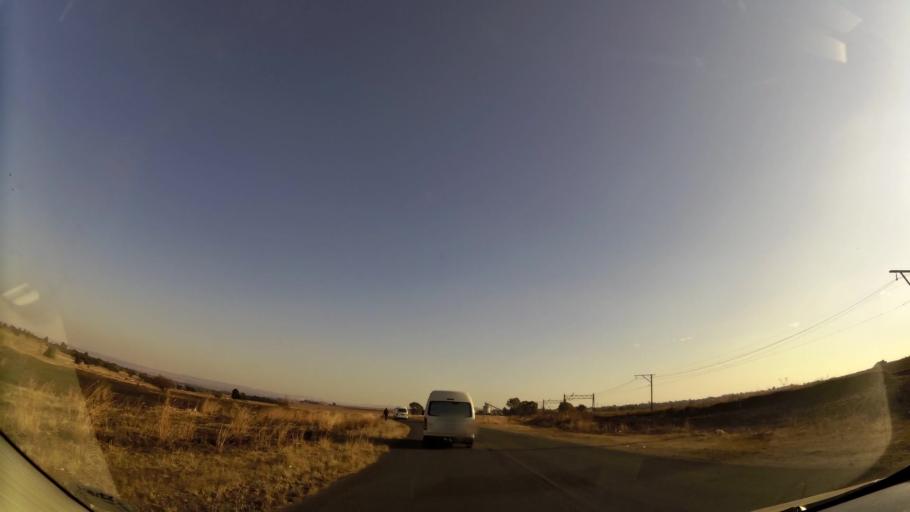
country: ZA
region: Gauteng
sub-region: West Rand District Municipality
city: Randfontein
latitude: -26.1992
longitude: 27.6755
